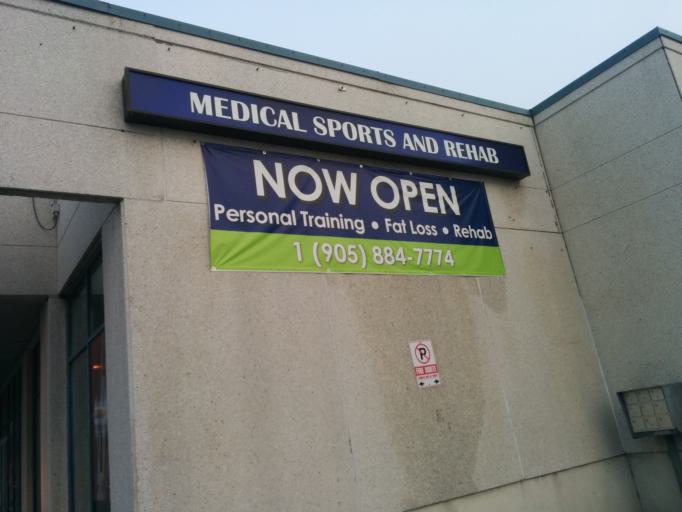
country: CA
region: Ontario
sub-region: York
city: Richmond Hill
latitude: 43.8944
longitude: -79.4413
